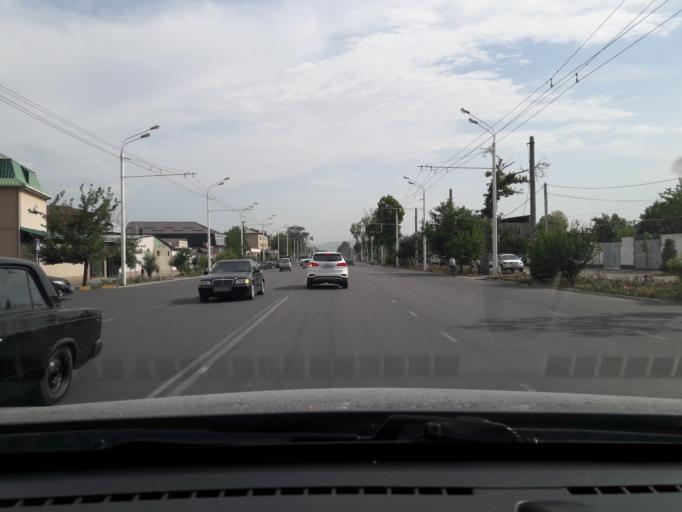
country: TJ
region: Dushanbe
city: Dushanbe
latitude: 38.5384
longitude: 68.7544
